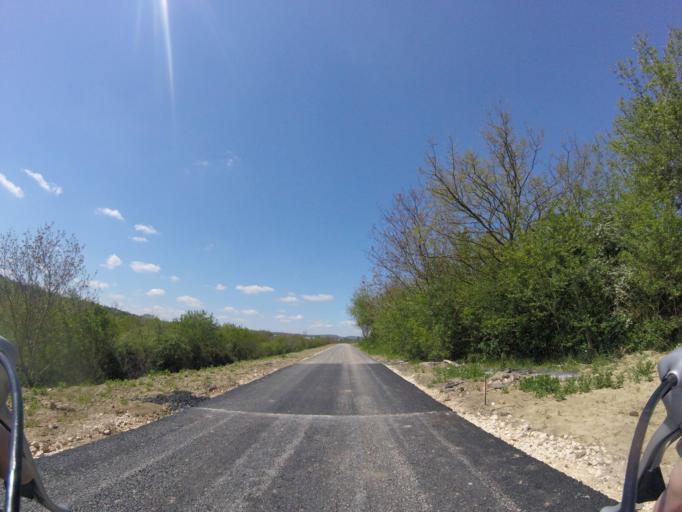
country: HU
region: Pest
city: Budaors
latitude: 47.4419
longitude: 18.9526
